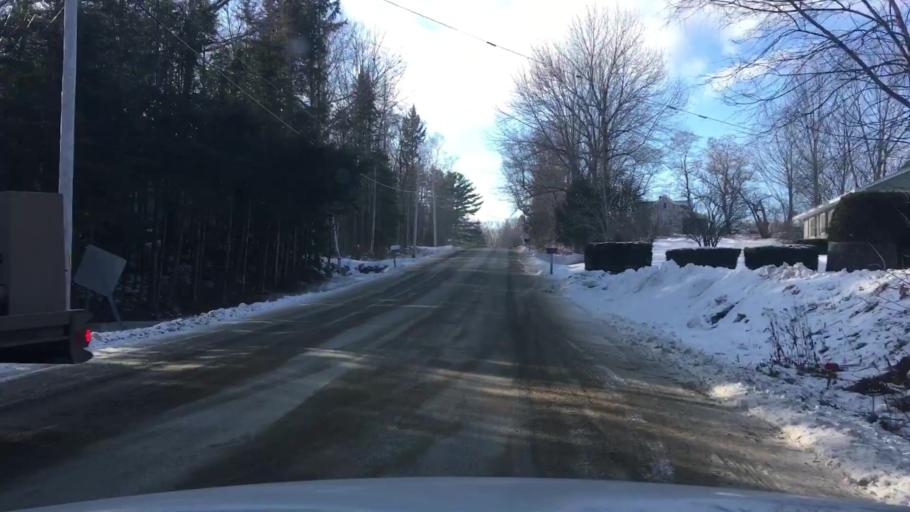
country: US
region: Maine
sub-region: Penobscot County
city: Eddington
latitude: 44.8286
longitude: -68.6501
